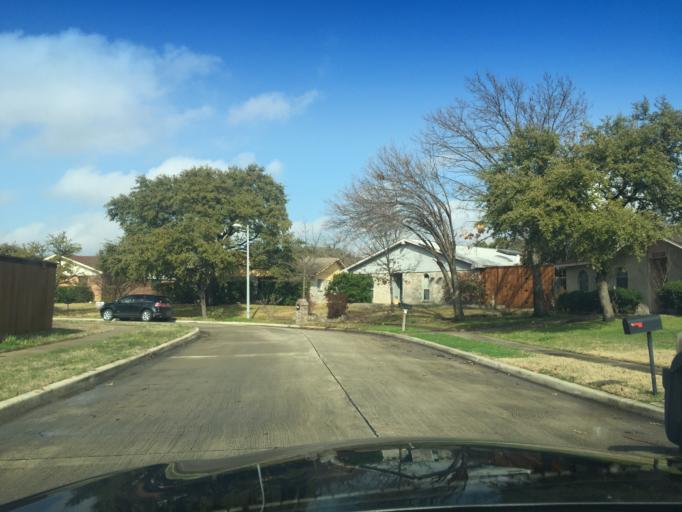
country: US
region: Texas
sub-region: Dallas County
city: Carrollton
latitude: 32.9942
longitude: -96.8752
